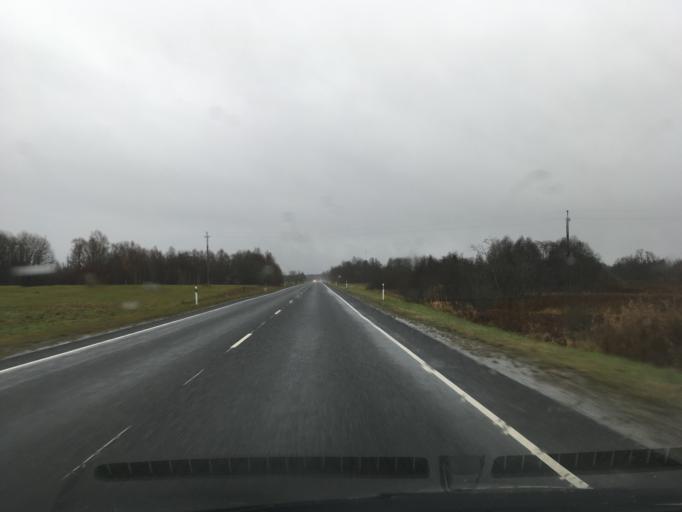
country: EE
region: Harju
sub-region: Nissi vald
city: Turba
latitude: 58.9163
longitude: 24.1123
